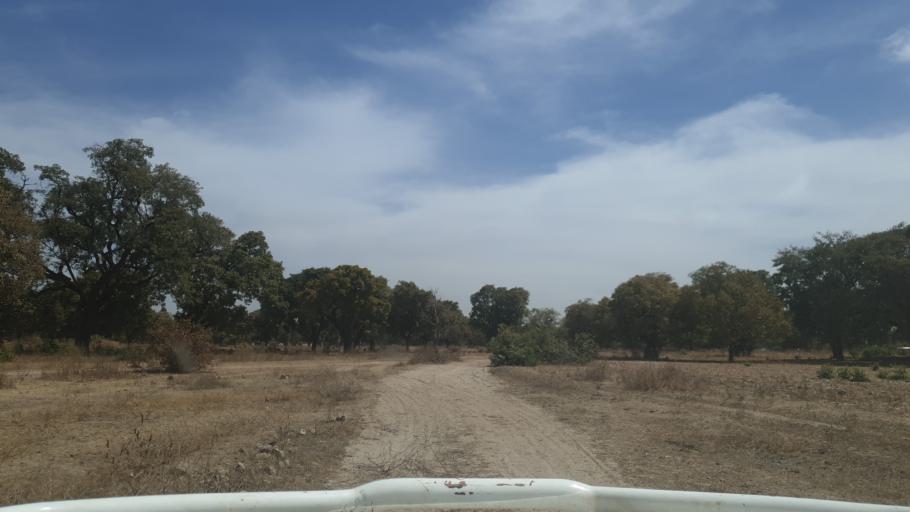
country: ML
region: Sikasso
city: Yorosso
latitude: 12.2922
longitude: -4.6620
